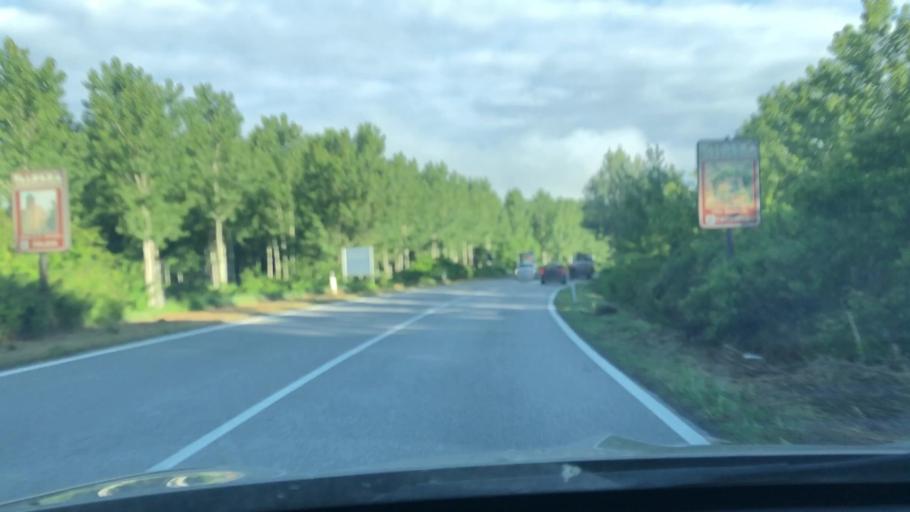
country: IT
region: Tuscany
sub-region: Province of Pisa
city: Forcoli
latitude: 43.6055
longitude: 10.6909
